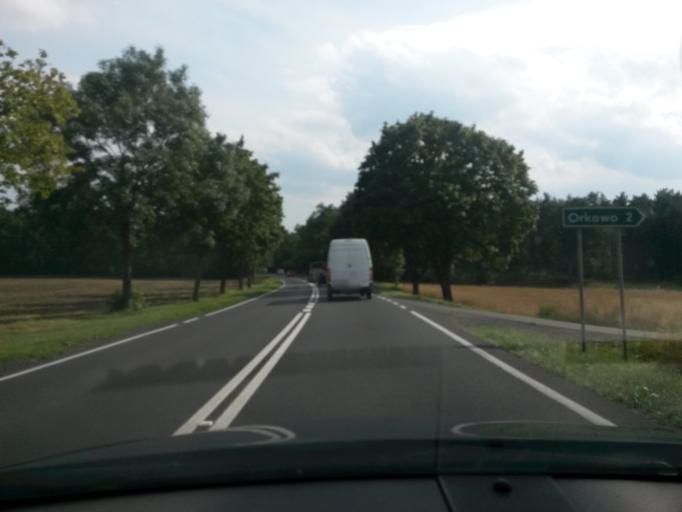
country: PL
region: Greater Poland Voivodeship
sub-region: Powiat sremski
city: Srem
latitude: 52.1542
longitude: 17.0349
